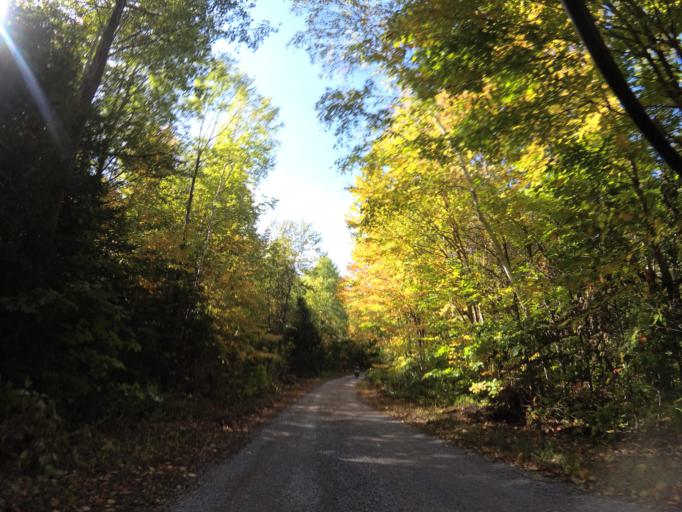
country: CA
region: Ontario
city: Renfrew
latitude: 45.3464
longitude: -77.0904
